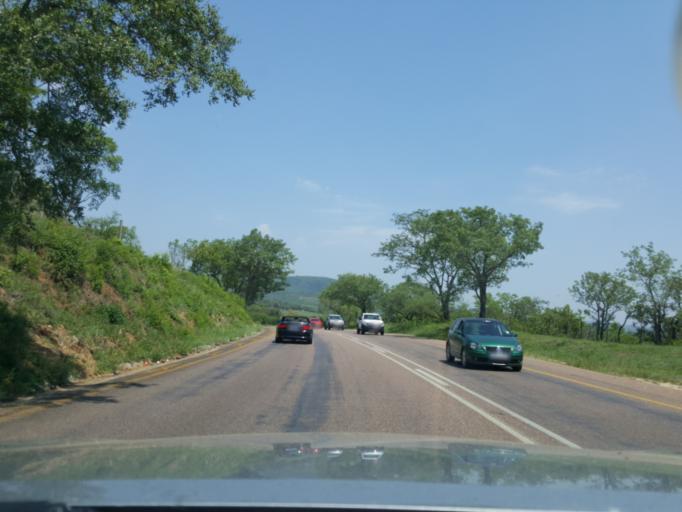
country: ZA
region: Mpumalanga
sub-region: Ehlanzeni District
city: Graksop
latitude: -25.0229
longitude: 31.1228
